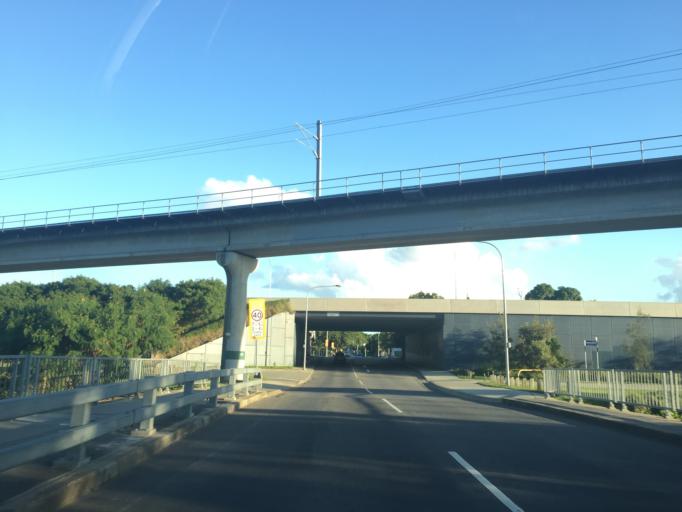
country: AU
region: Queensland
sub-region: Brisbane
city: Ascot
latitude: -27.4109
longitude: 153.0635
